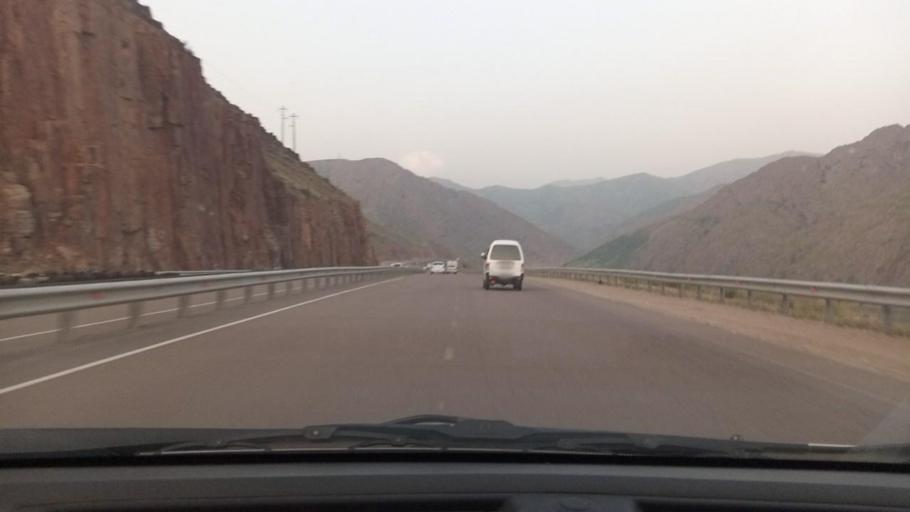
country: UZ
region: Toshkent
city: Angren
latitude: 41.0724
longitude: 70.2771
